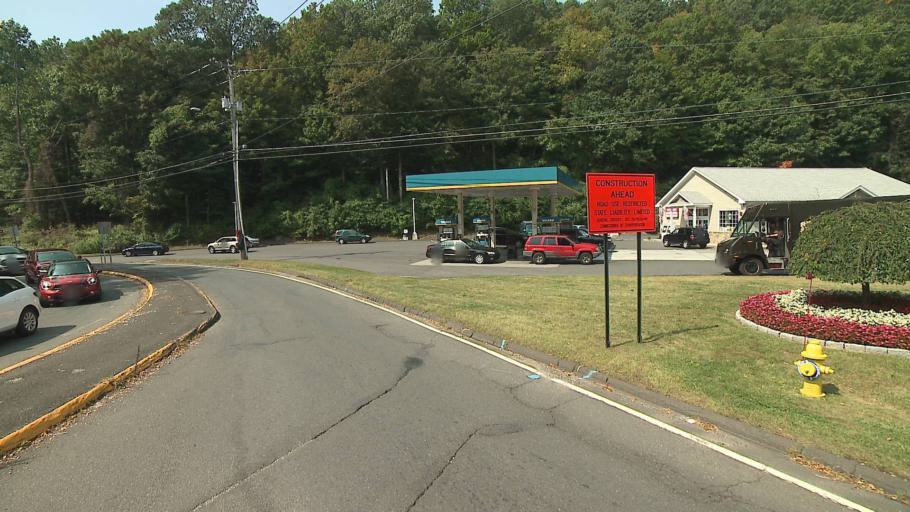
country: US
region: Connecticut
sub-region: Fairfield County
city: Ridgefield
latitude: 41.3216
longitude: -73.4762
